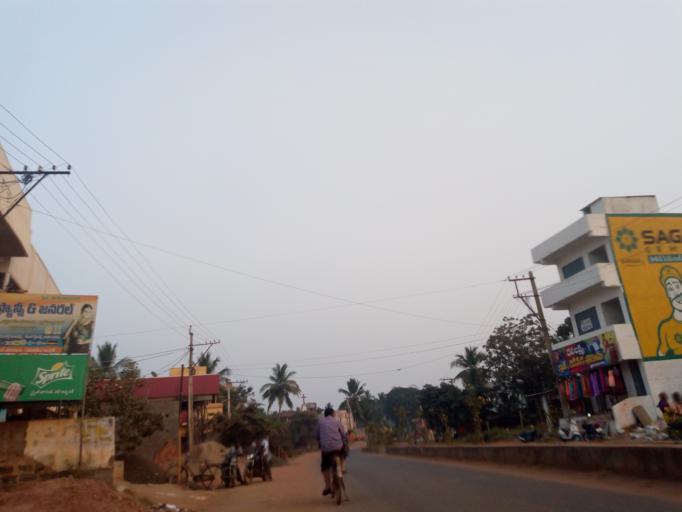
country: IN
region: Andhra Pradesh
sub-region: West Godavari
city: Eluru
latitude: 16.8216
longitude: 81.2636
